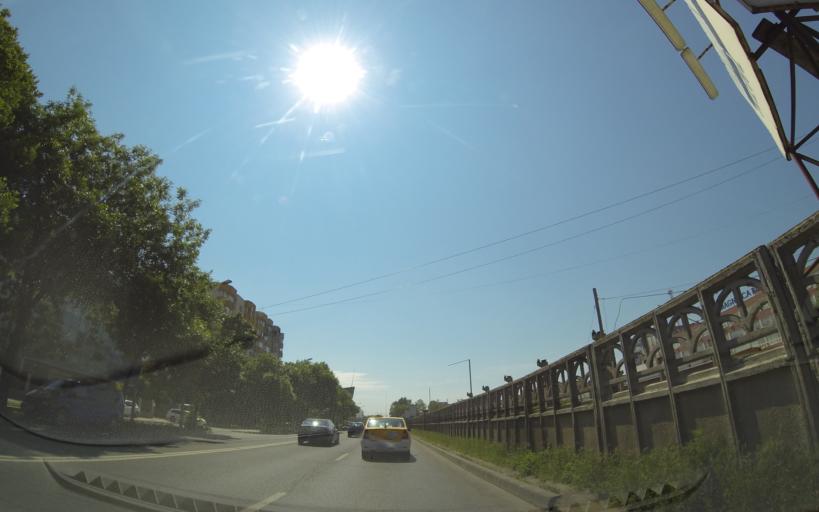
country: RO
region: Bucuresti
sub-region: Municipiul Bucuresti
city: Bucuresti
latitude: 44.4170
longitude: 26.0766
